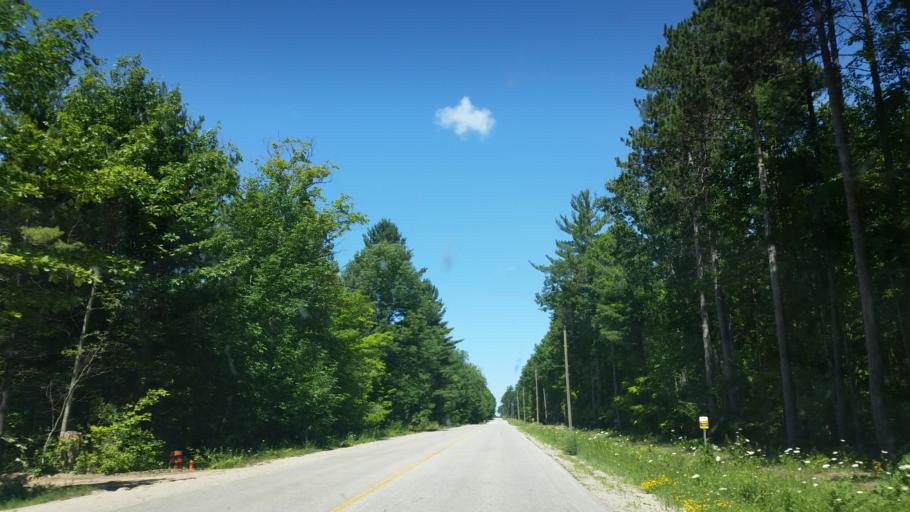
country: CA
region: Ontario
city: Barrie
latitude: 44.4737
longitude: -79.8064
